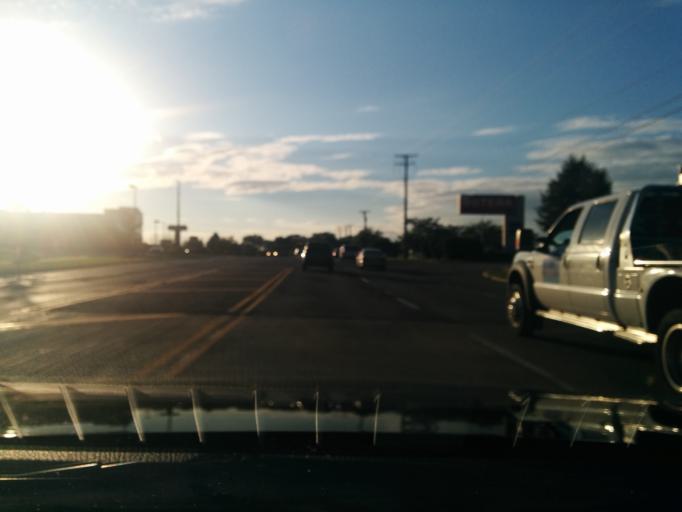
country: US
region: Illinois
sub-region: DuPage County
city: Bloomingdale
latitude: 41.9633
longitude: -88.0970
